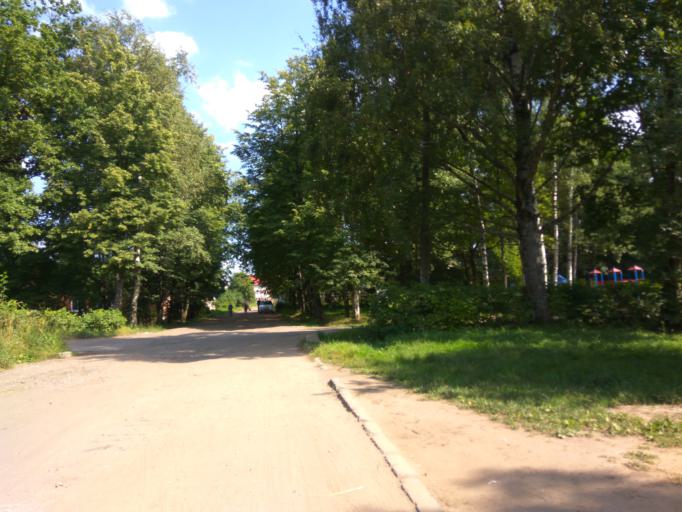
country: RU
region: Moskovskaya
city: Kubinka
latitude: 55.5796
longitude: 36.7693
